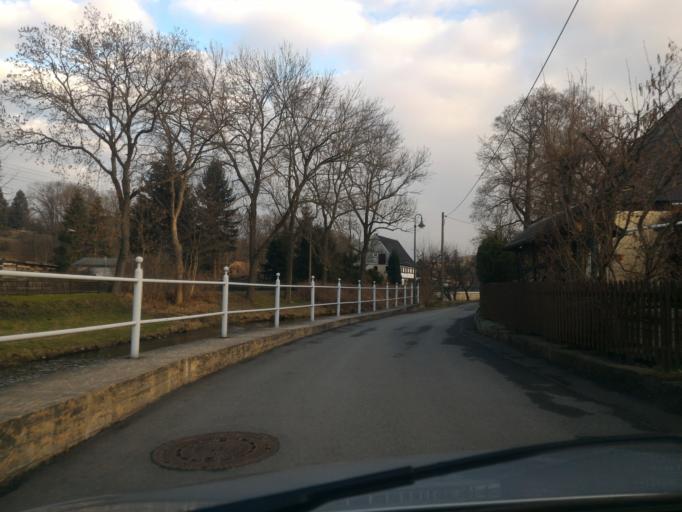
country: DE
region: Saxony
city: Grossschonau
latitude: 50.8961
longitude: 14.6781
